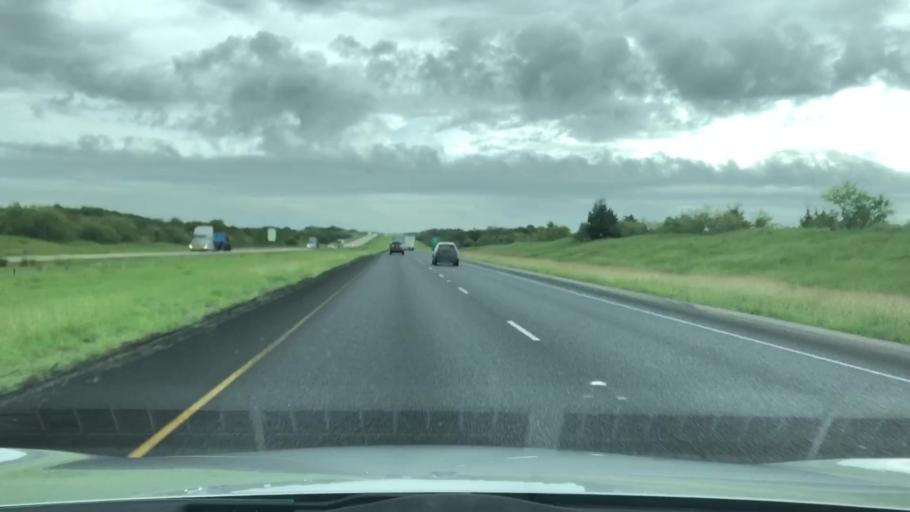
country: US
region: Texas
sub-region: Gonzales County
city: Waelder
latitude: 29.6666
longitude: -97.3283
